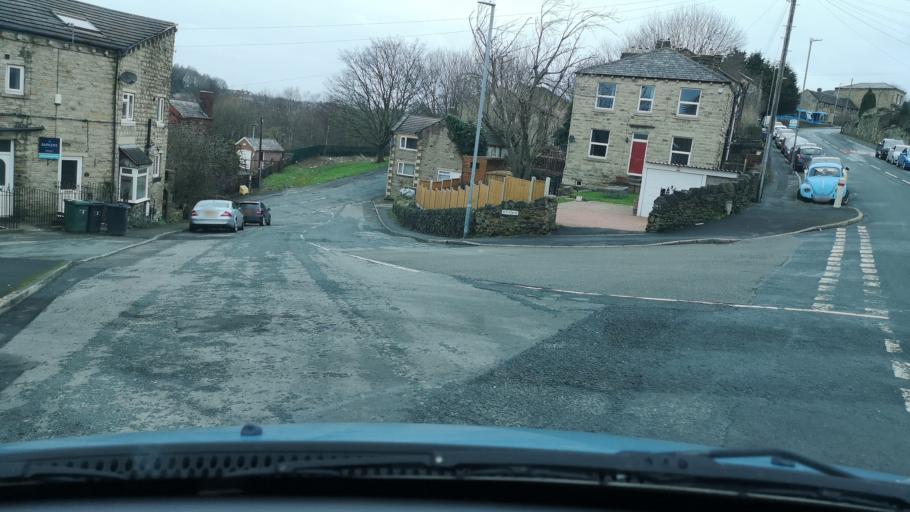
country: GB
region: England
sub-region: Kirklees
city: Batley
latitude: 53.7017
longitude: -1.6270
